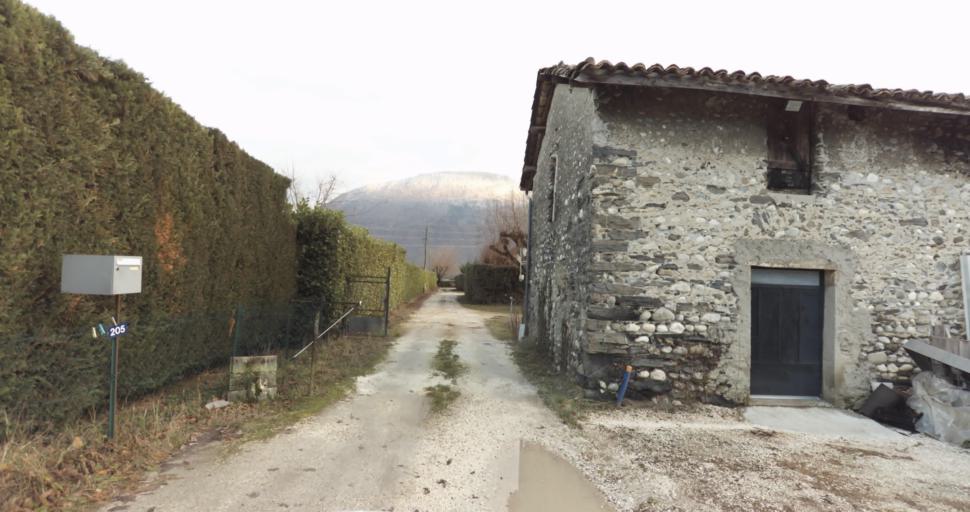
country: FR
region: Rhone-Alpes
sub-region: Departement de l'Isere
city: Allieres-et-Risset
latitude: 45.0770
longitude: 5.6963
